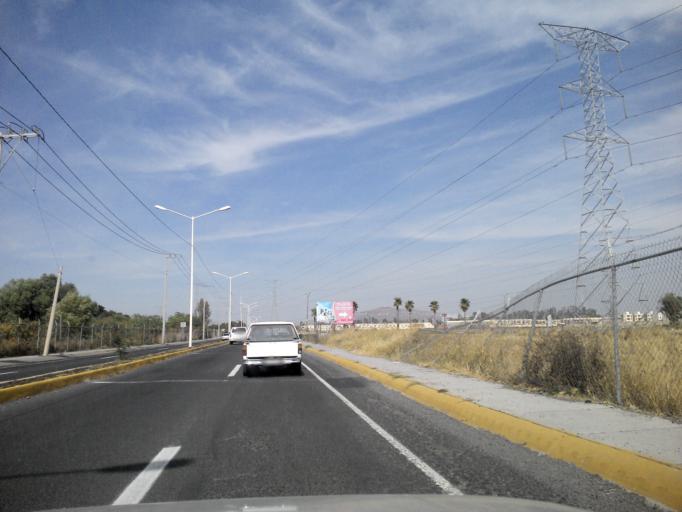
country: MX
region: Jalisco
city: San Sebastian el Grande
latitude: 20.5270
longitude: -103.4077
